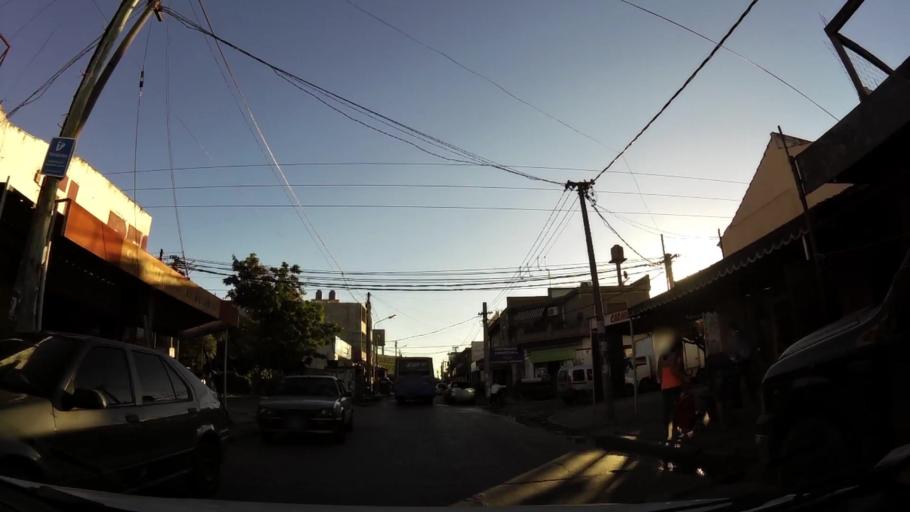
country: AR
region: Buenos Aires
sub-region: Partido de Moron
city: Moron
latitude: -34.7136
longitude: -58.6129
